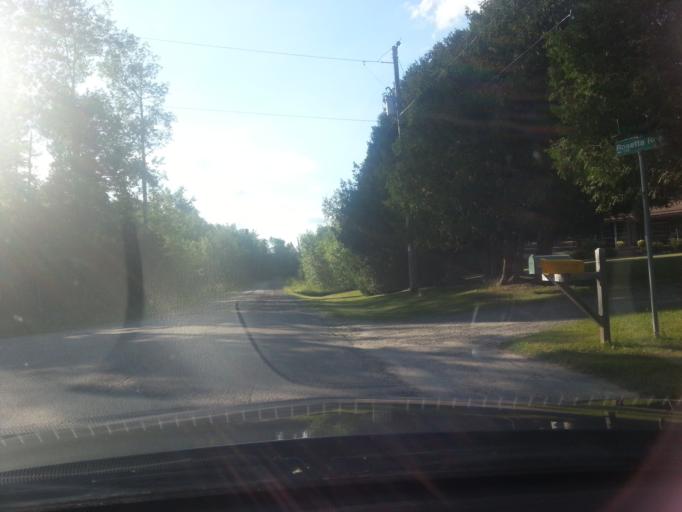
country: CA
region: Ontario
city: Perth
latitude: 45.0261
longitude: -76.3634
